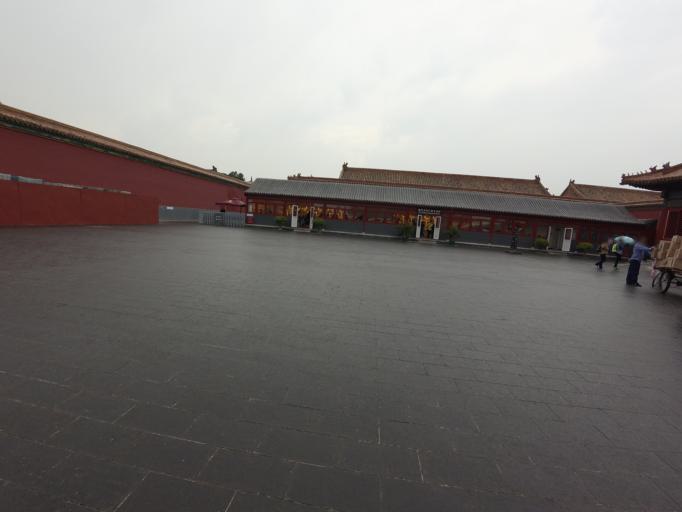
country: CN
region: Beijing
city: Beijing
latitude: 39.9173
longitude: 116.3891
